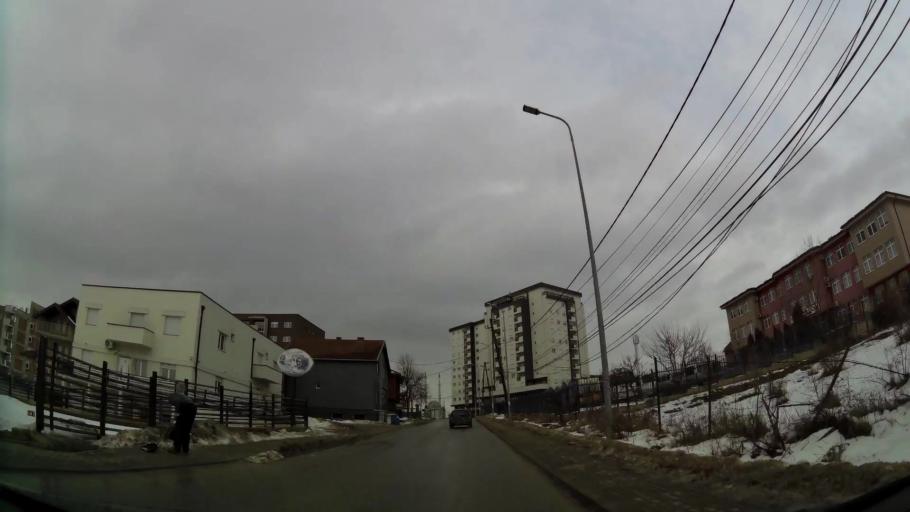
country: XK
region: Pristina
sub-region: Komuna e Prishtines
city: Pristina
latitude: 42.6536
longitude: 21.1913
